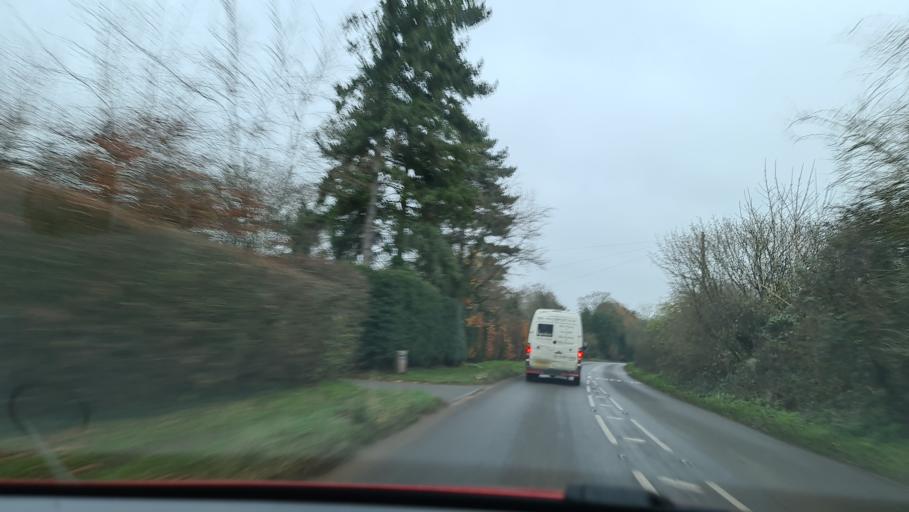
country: GB
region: England
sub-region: Buckinghamshire
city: Seer Green
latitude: 51.6112
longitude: -0.6048
